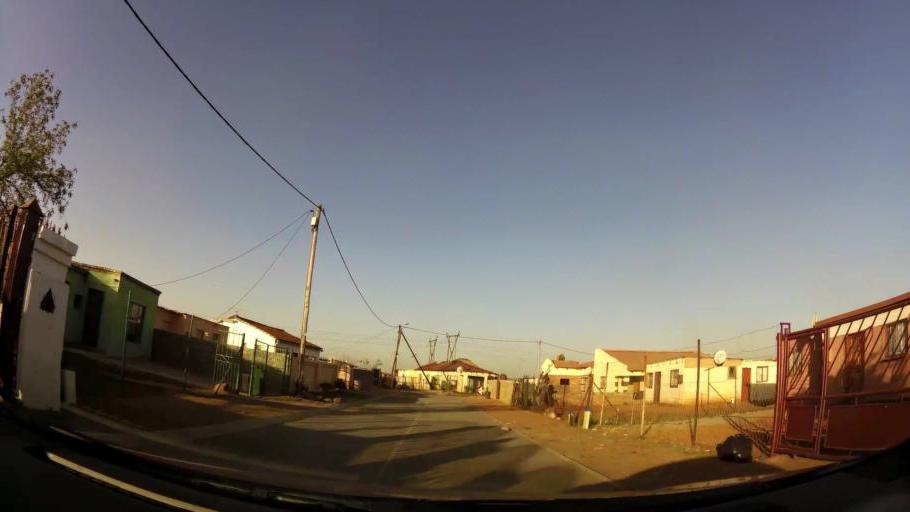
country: ZA
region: Gauteng
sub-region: City of Tshwane Metropolitan Municipality
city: Mabopane
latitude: -25.6030
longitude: 28.1061
